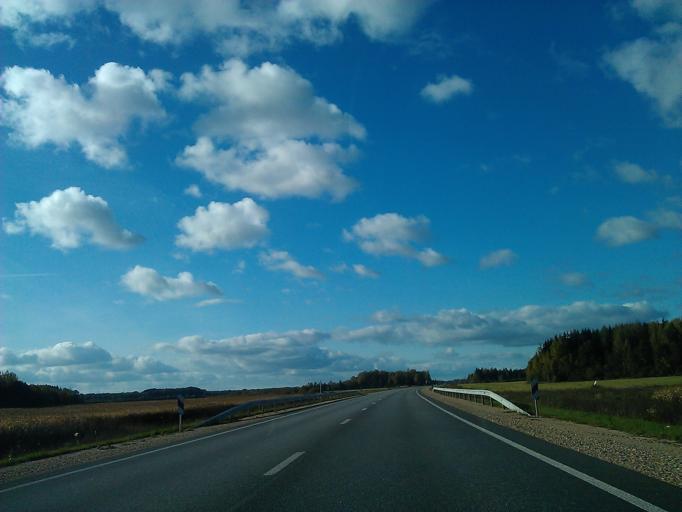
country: LV
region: Koknese
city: Koknese
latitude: 56.6712
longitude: 25.4010
